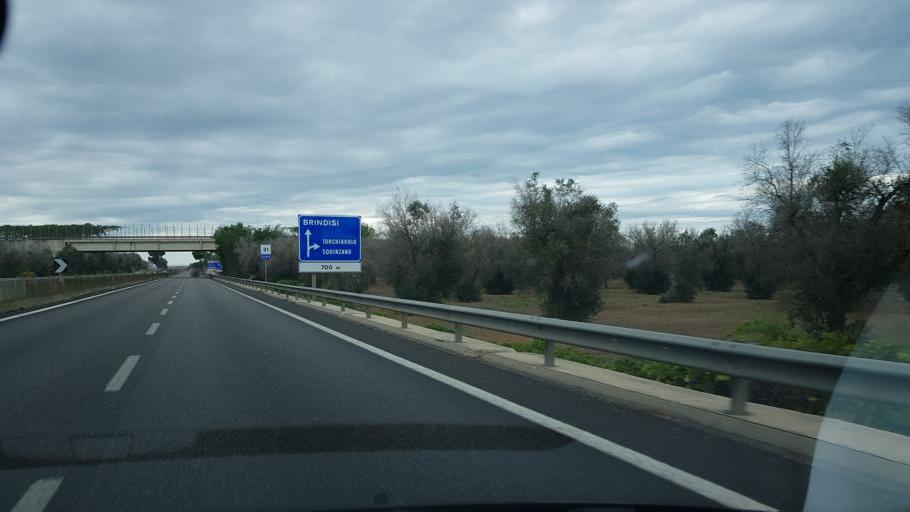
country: IT
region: Apulia
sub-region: Provincia di Lecce
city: Squinzano
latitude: 40.4552
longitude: 18.0638
